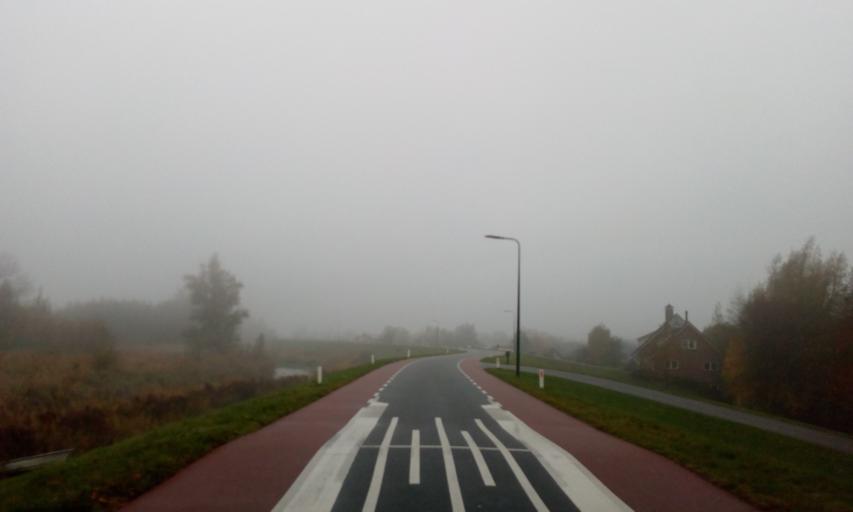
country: NL
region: South Holland
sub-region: Molenwaard
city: Liesveld
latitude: 51.9329
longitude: 4.8152
